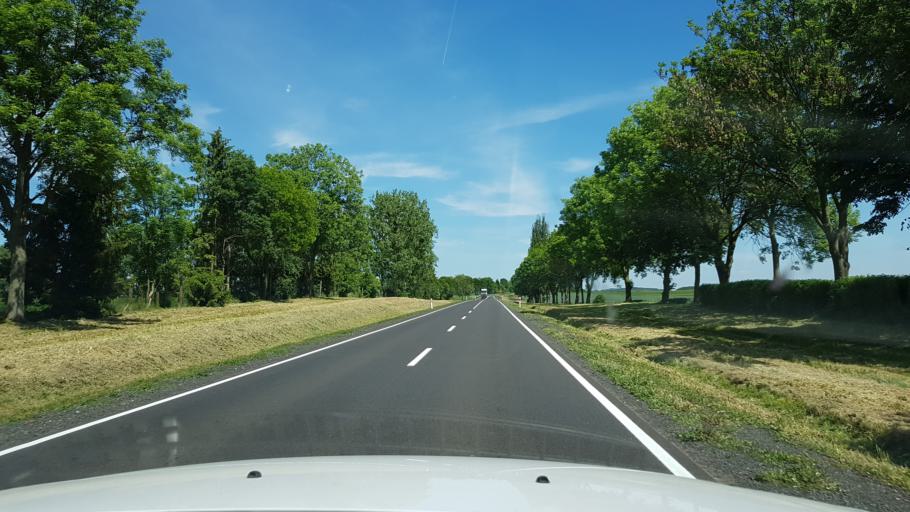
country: PL
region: West Pomeranian Voivodeship
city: Trzcinsko Zdroj
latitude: 52.9604
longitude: 14.5560
